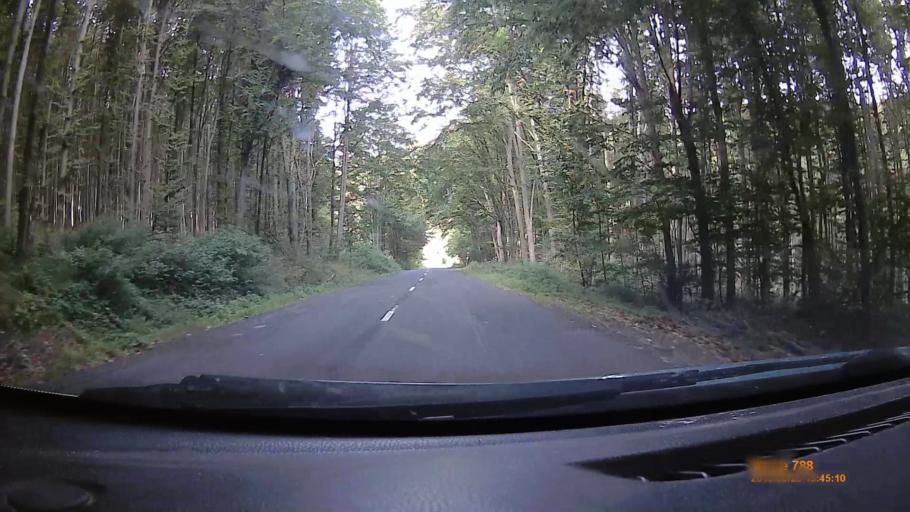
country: HU
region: Borsod-Abauj-Zemplen
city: Saly
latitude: 48.0632
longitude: 20.5637
